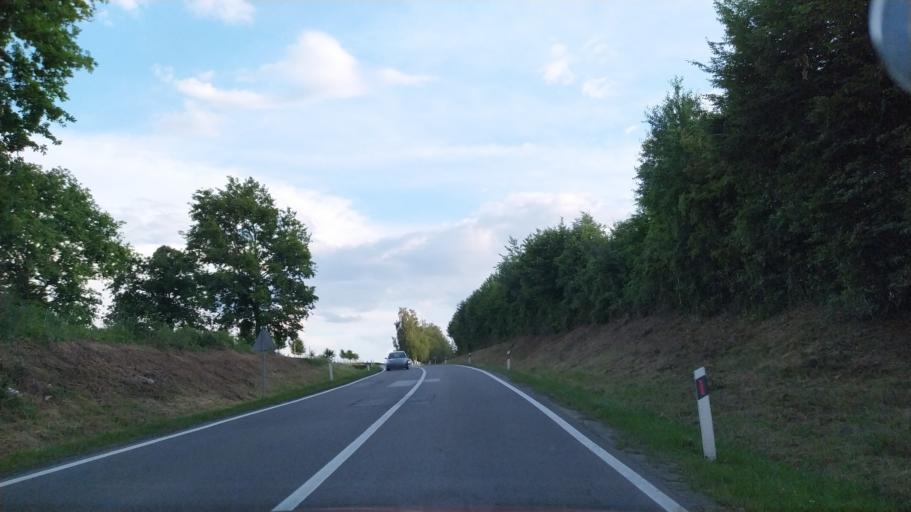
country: HR
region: Osjecko-Baranjska
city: Fericanci
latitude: 45.5054
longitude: 18.0132
